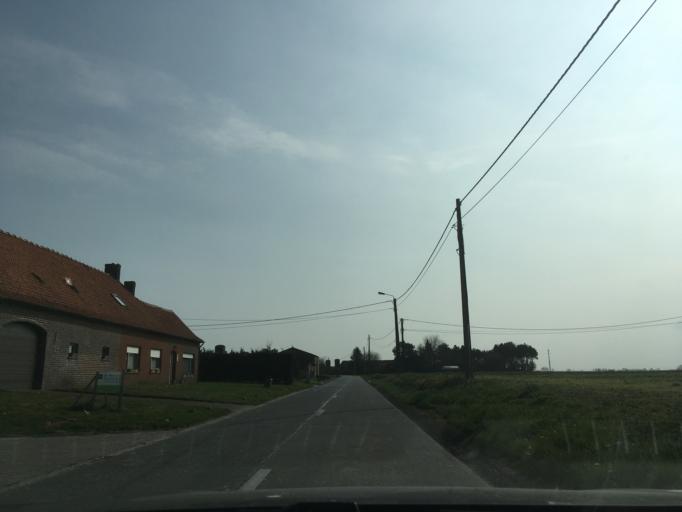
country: BE
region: Flanders
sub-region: Provincie West-Vlaanderen
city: Lichtervelde
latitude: 51.0232
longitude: 3.1817
